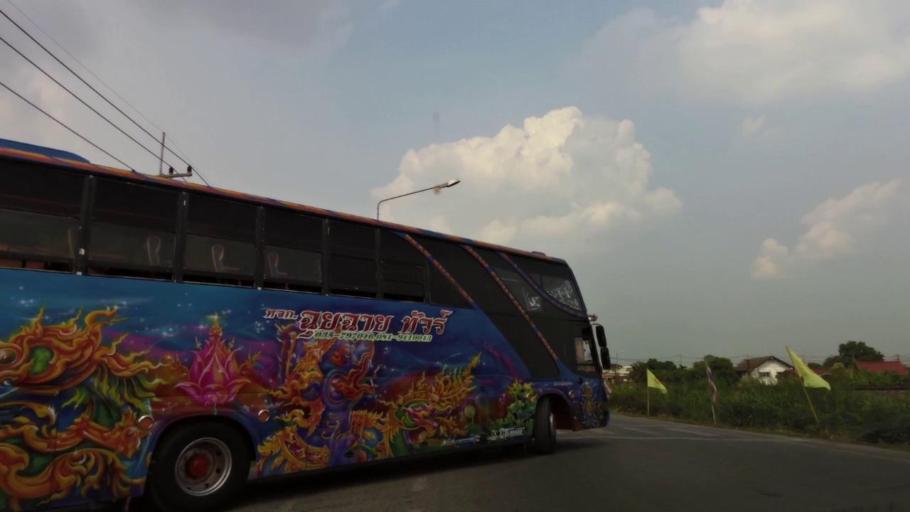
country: TH
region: Phra Nakhon Si Ayutthaya
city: Phra Nakhon Si Ayutthaya
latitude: 14.3372
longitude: 100.5819
